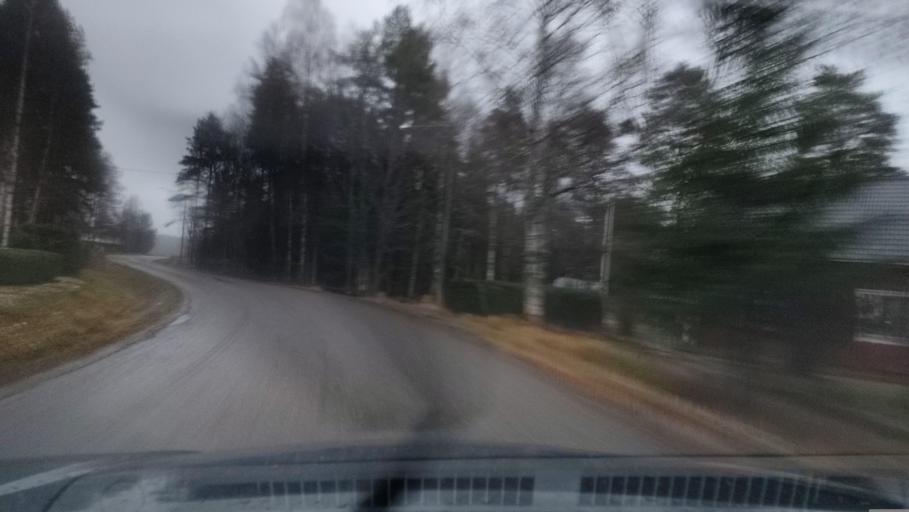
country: FI
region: Southern Ostrobothnia
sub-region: Suupohja
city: Karijoki
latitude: 62.1287
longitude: 21.5813
